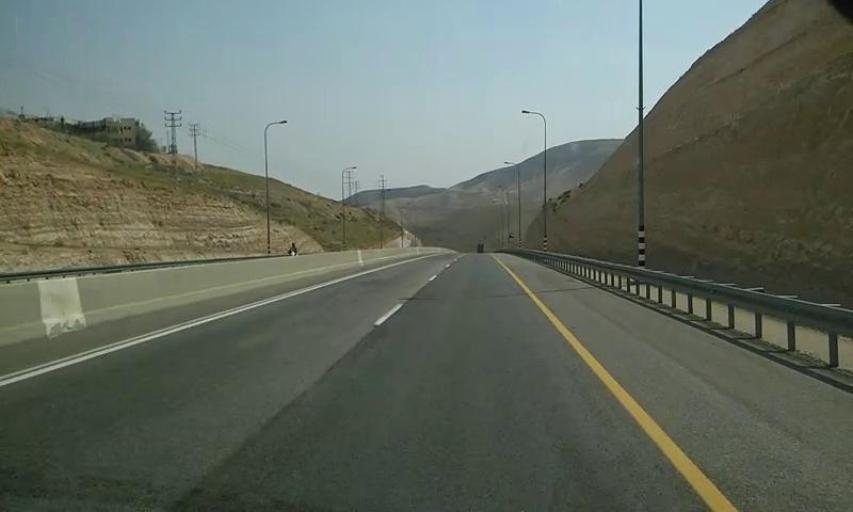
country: PS
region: West Bank
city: Jericho
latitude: 31.8143
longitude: 35.3899
